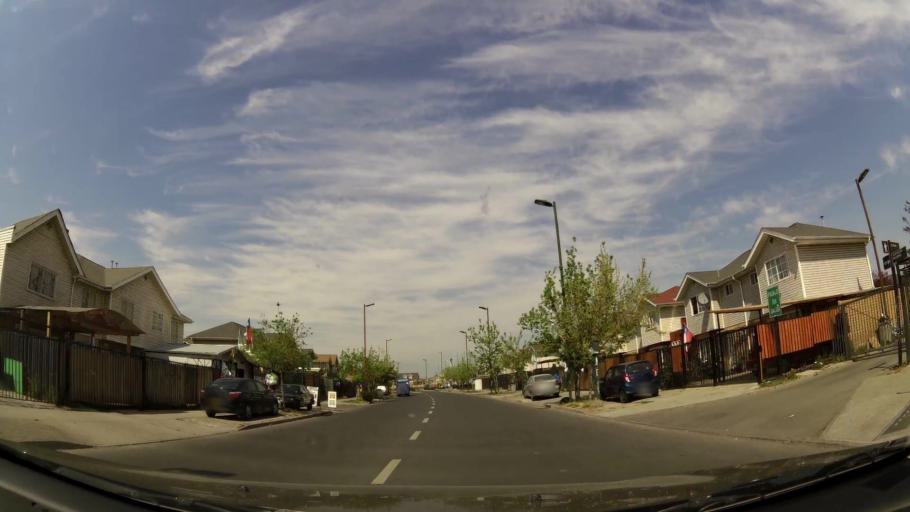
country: CL
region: Santiago Metropolitan
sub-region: Provincia de Cordillera
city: Puente Alto
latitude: -33.5943
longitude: -70.5904
